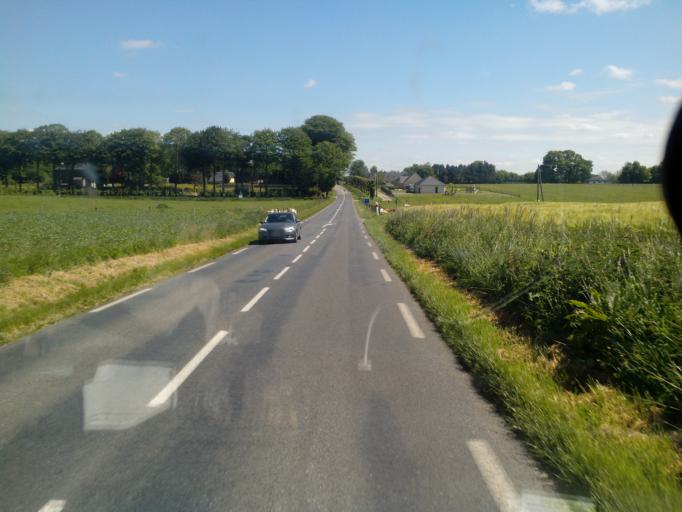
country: FR
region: Haute-Normandie
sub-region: Departement de la Seine-Maritime
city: Turretot
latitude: 49.6241
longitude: 0.2772
